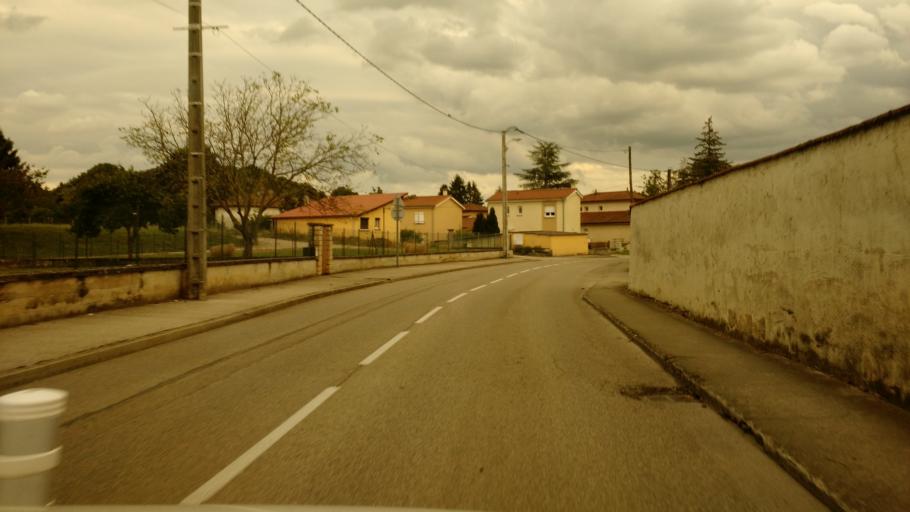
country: FR
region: Rhone-Alpes
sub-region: Departement de l'Ain
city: Montluel
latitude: 45.8563
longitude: 5.0583
